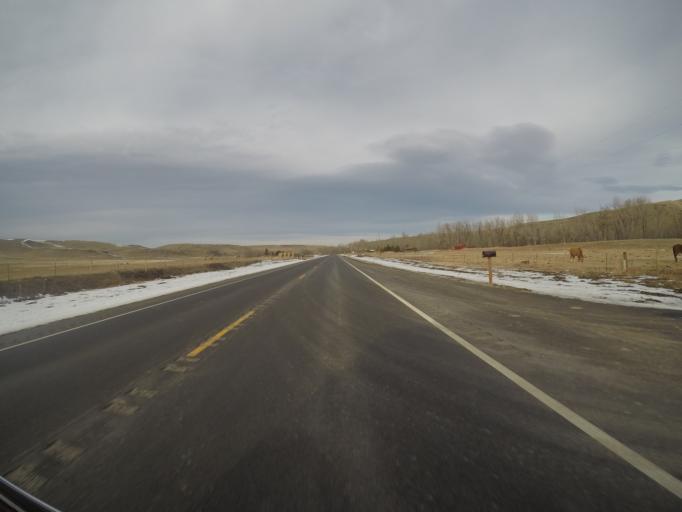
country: US
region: Montana
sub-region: Stillwater County
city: Absarokee
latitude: 45.4245
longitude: -109.4712
